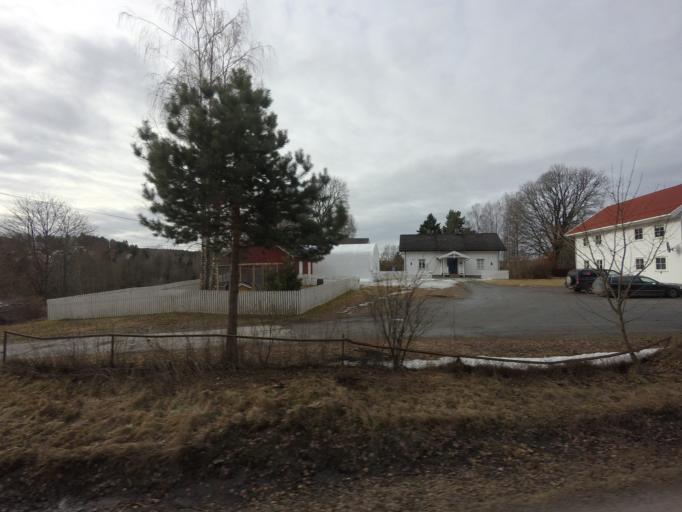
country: NO
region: Akershus
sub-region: Enebakk
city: Flateby
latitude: 59.8558
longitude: 11.2341
